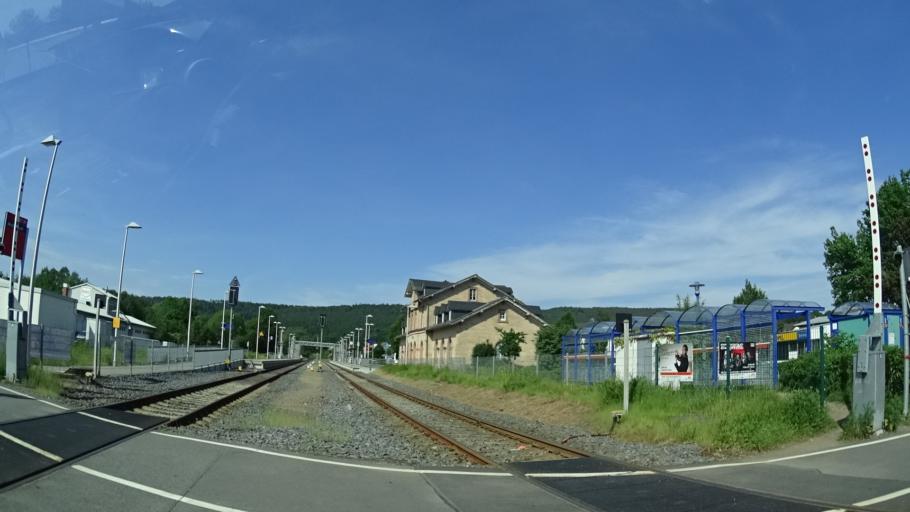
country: DE
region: Hesse
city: Michelstadt
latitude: 49.6840
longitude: 9.0006
